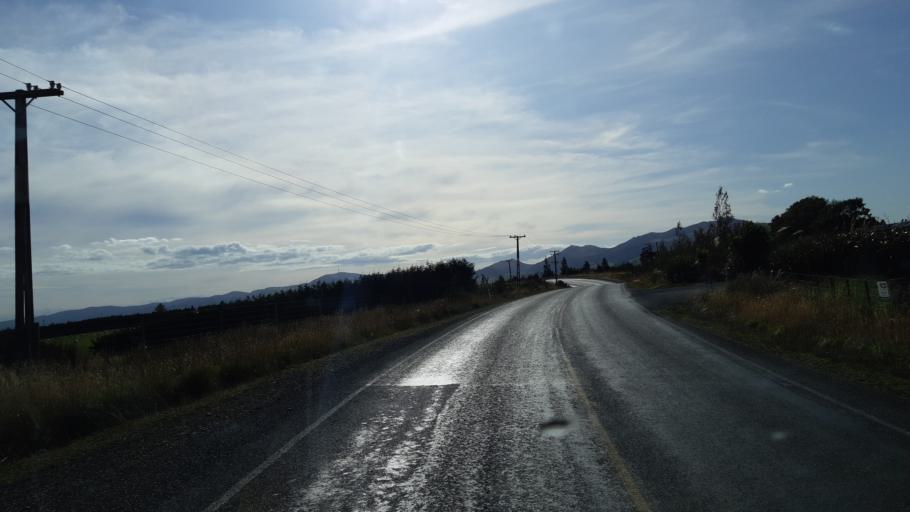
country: NZ
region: Southland
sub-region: Gore District
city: Gore
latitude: -46.1099
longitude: 168.8634
